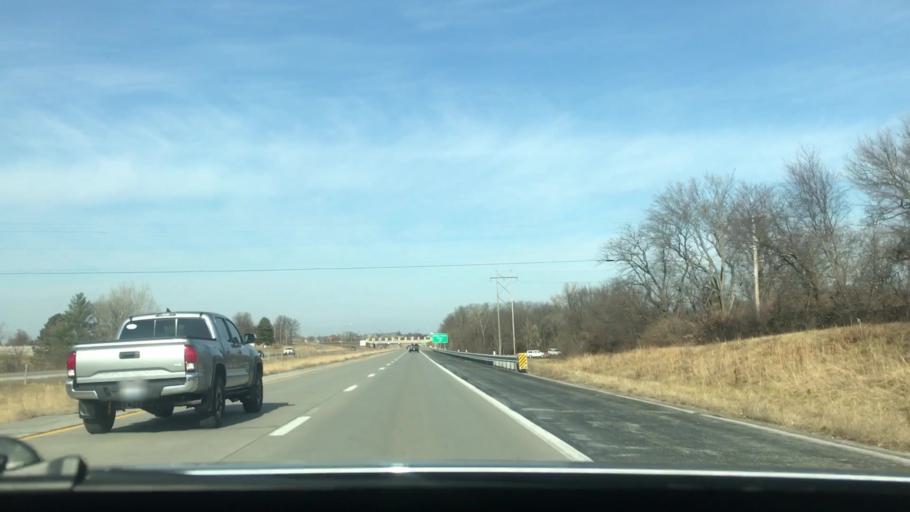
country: US
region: Missouri
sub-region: Clay County
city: Gladstone
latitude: 39.2814
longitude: -94.5849
